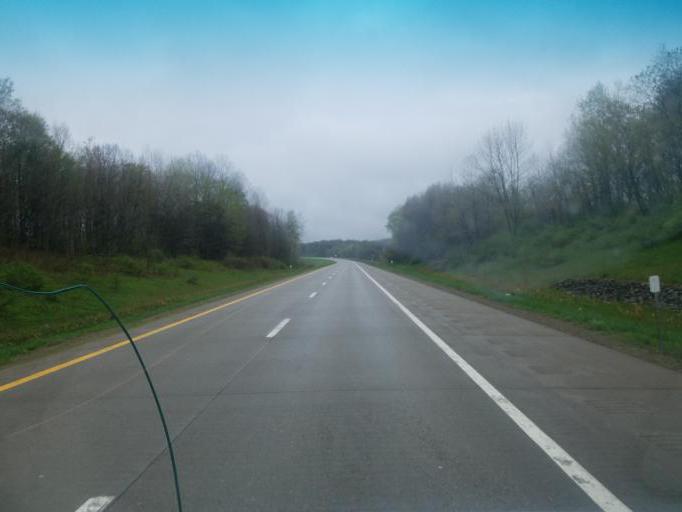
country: US
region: New York
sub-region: Chautauqua County
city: Clymer
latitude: 42.1449
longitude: -79.6947
